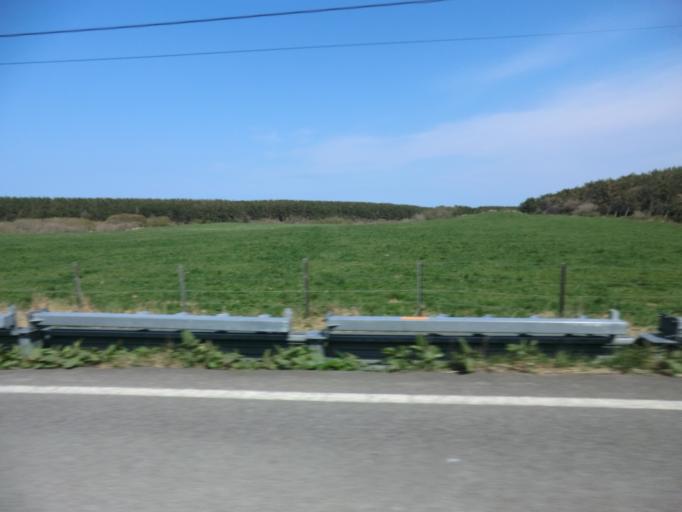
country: JP
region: Aomori
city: Mutsu
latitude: 41.4100
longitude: 141.4486
